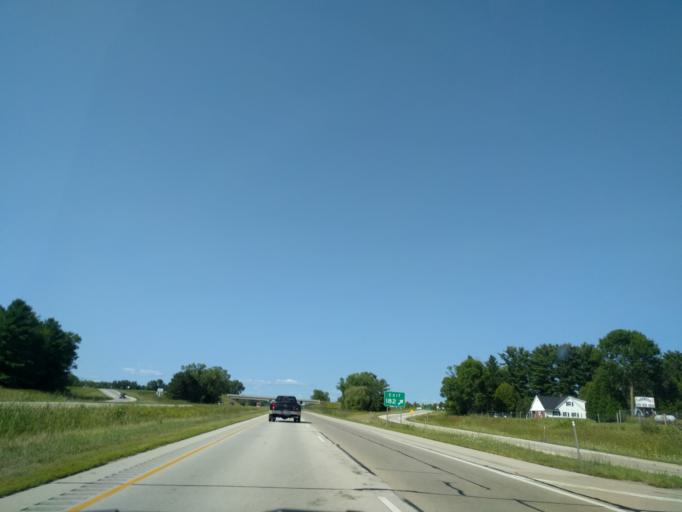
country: US
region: Wisconsin
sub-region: Brown County
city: Suamico
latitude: 44.7174
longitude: -88.0508
